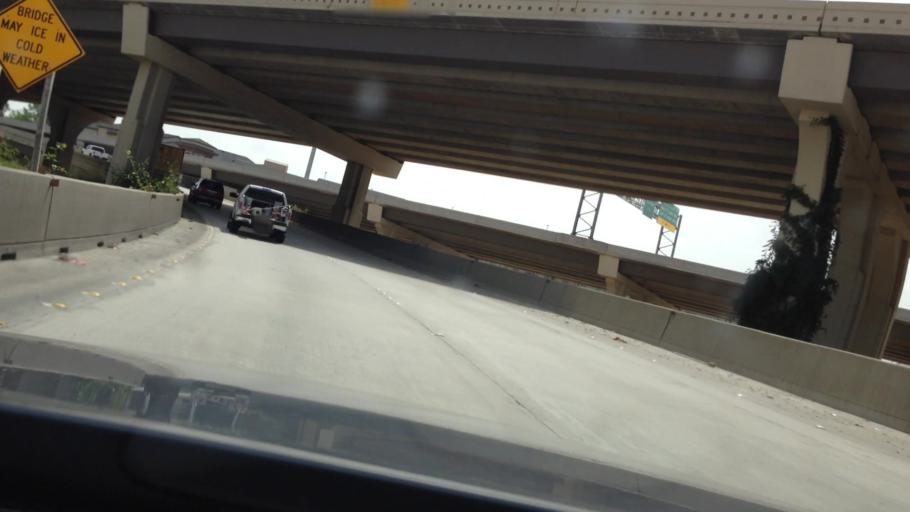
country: US
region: Texas
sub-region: Harris County
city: Spring Valley
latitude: 29.8028
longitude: -95.4498
